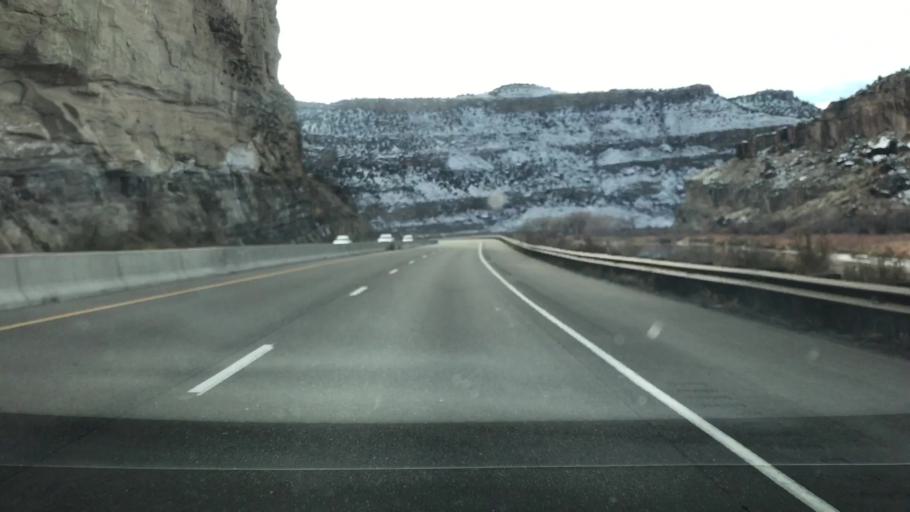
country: US
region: Colorado
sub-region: Mesa County
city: Palisade
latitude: 39.2479
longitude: -108.2564
